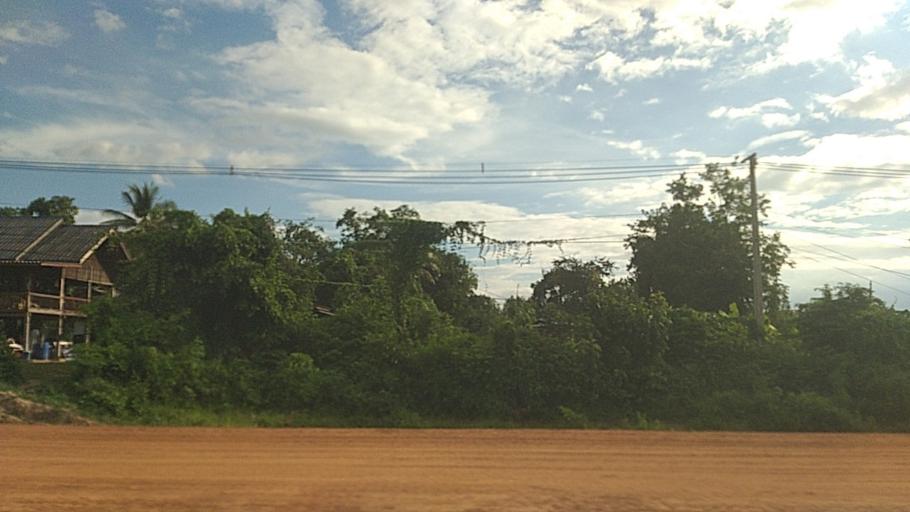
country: TH
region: Surin
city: Kap Choeng
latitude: 14.5011
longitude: 103.5628
